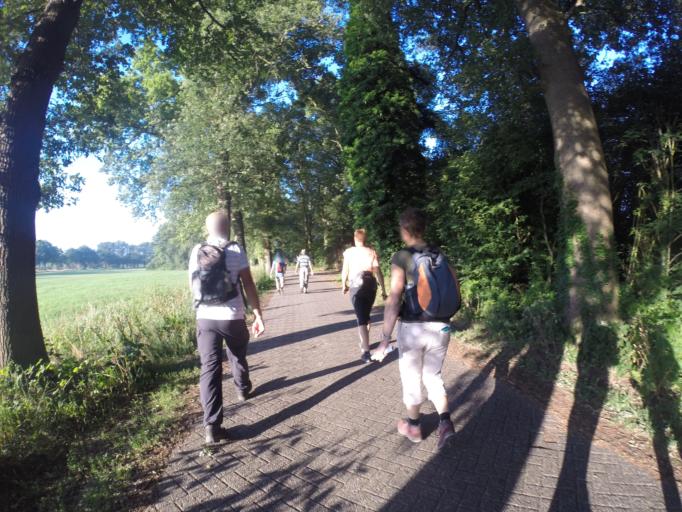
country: NL
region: Gelderland
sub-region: Gemeente Lochem
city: Barchem
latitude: 52.1221
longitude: 6.4334
